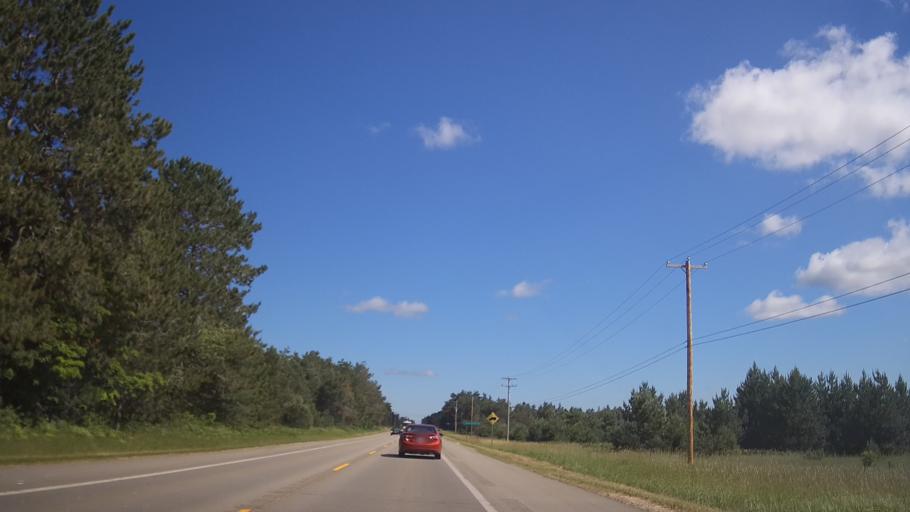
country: US
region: Michigan
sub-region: Cheboygan County
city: Indian River
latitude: 45.4832
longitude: -84.7811
